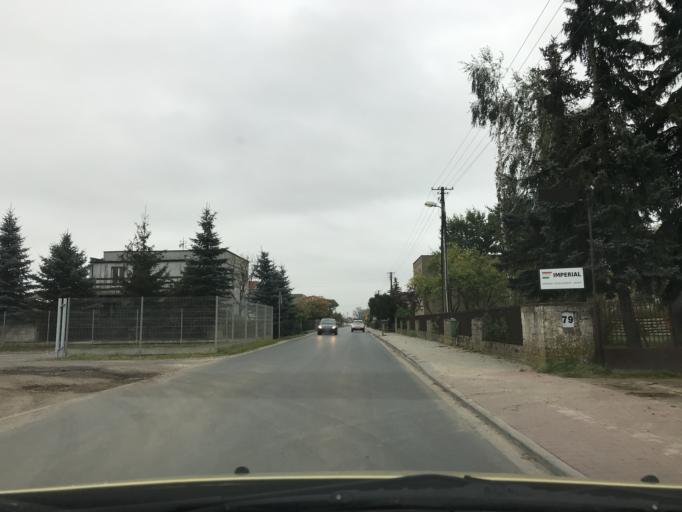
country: PL
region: Greater Poland Voivodeship
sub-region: Powiat poznanski
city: Baranowo
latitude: 52.4073
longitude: 16.7358
